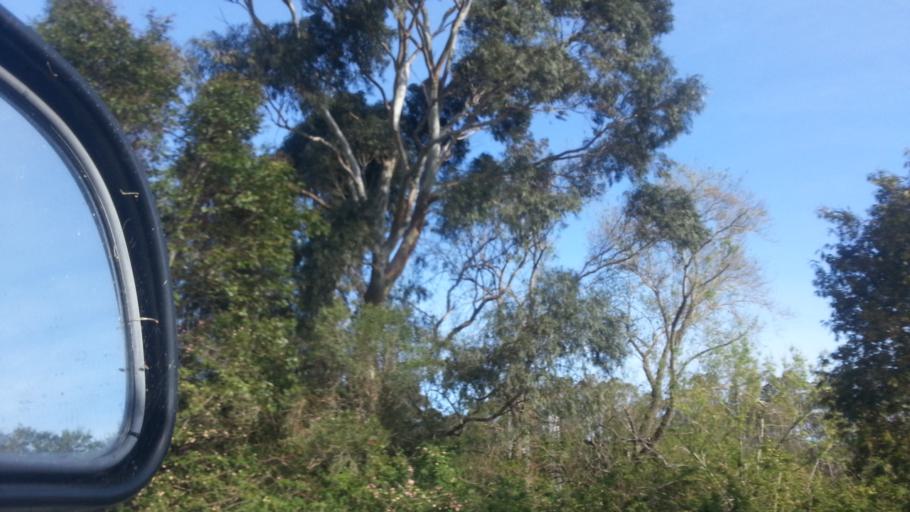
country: AU
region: New South Wales
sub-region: Wollongong
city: Mount Saint Thomas
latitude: -34.4439
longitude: 150.8670
